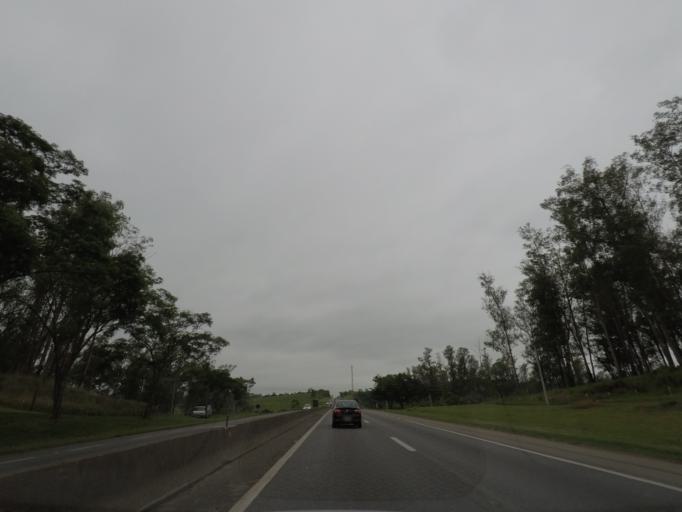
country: BR
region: Sao Paulo
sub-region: Pindamonhangaba
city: Pindamonhangaba
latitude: -22.9763
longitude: -45.4524
